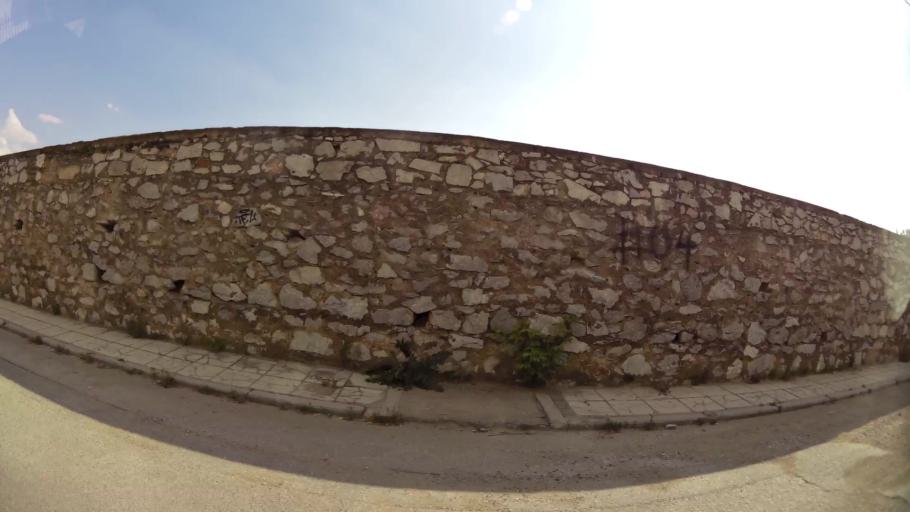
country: GR
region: Central Macedonia
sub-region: Nomos Thessalonikis
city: Polichni
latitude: 40.6635
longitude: 22.9507
